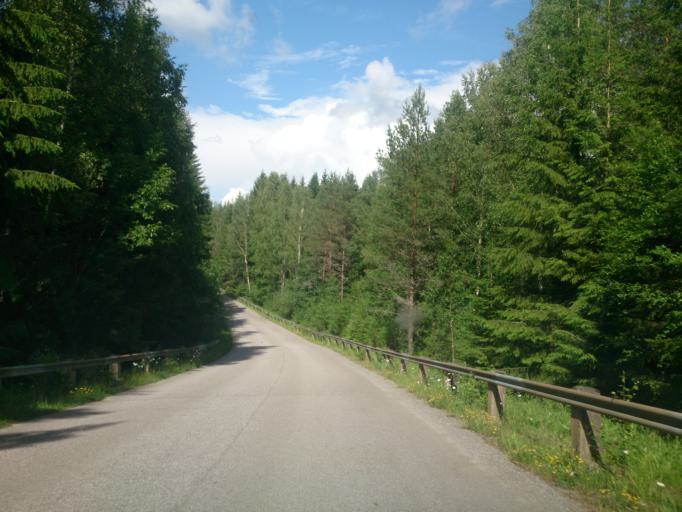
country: SE
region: OEstergoetland
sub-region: Norrkopings Kommun
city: Jursla
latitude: 58.7226
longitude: 16.0920
